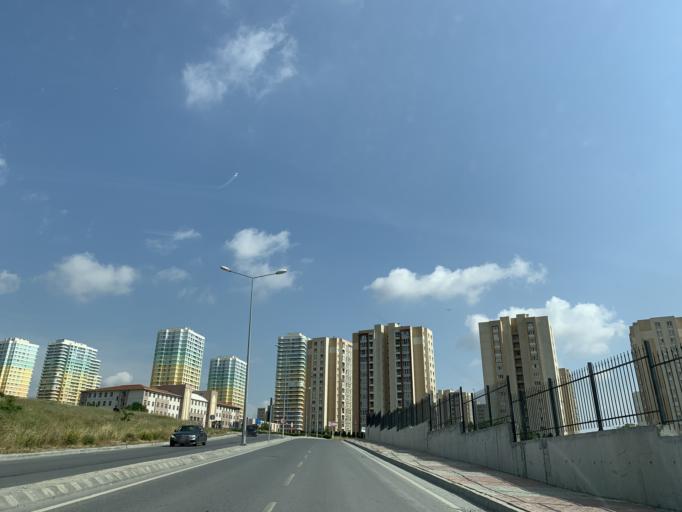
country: TR
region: Istanbul
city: Esenyurt
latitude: 41.0665
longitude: 28.7055
